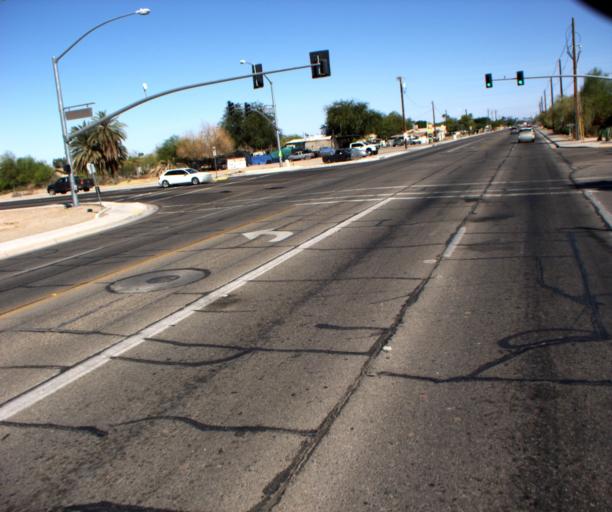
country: US
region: Arizona
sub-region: Yuma County
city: Yuma
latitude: 32.6763
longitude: -114.6502
